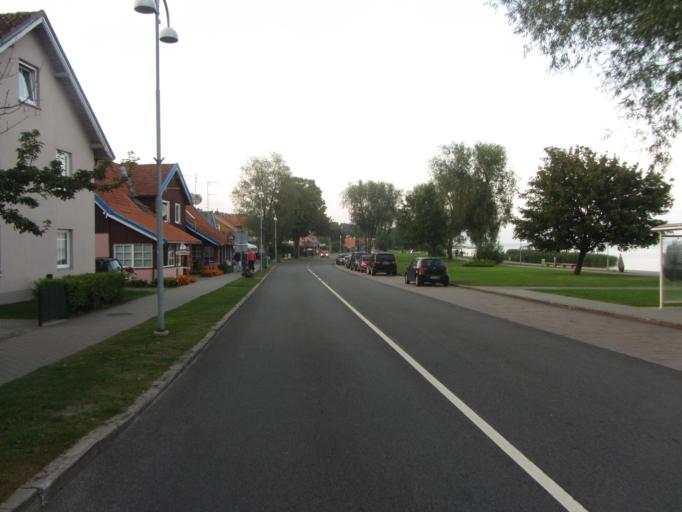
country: LT
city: Neringa
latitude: 55.5361
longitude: 21.1177
